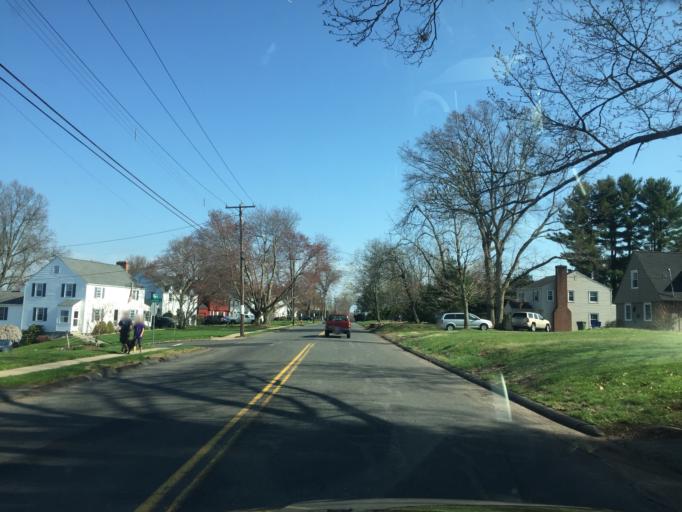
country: US
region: Connecticut
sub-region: Hartford County
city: Wethersfield
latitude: 41.6957
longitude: -72.6826
